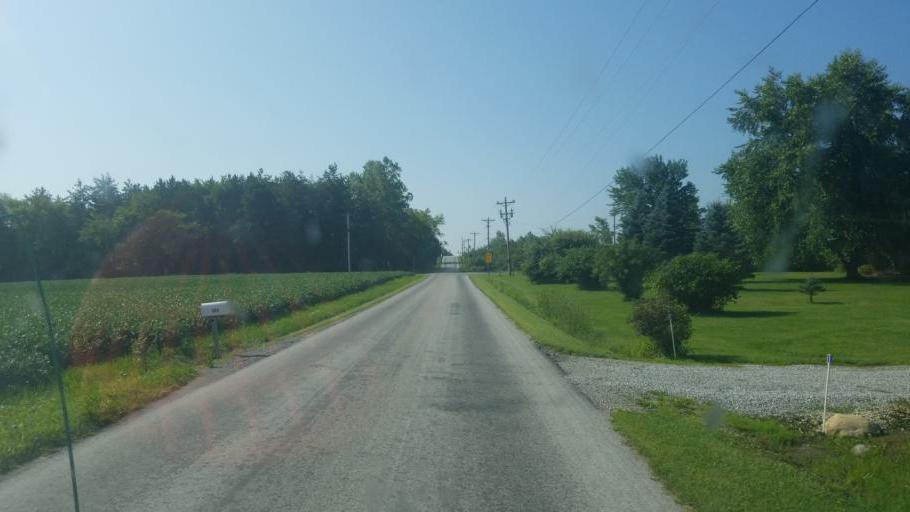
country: US
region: Ohio
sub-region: Wayne County
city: West Salem
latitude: 41.0437
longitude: -82.2017
